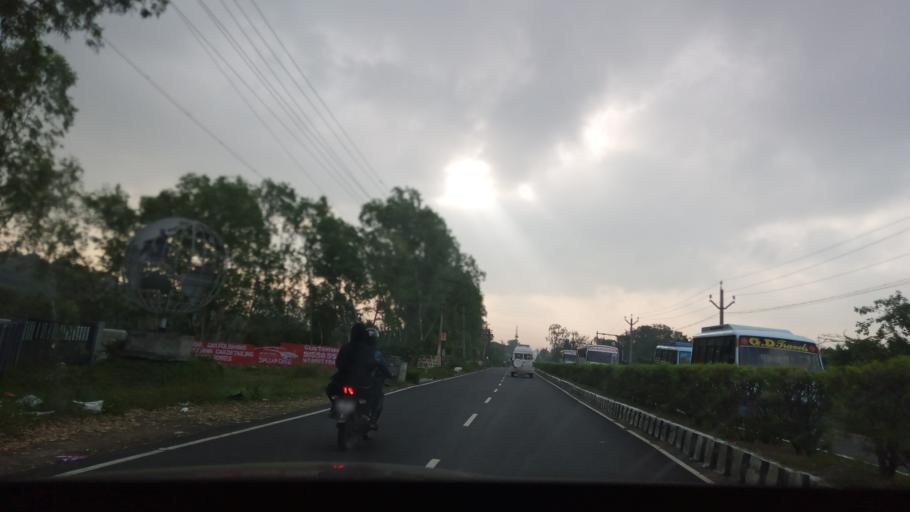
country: IN
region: Tamil Nadu
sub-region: Kancheepuram
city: Vengavasal
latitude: 12.8089
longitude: 80.1860
